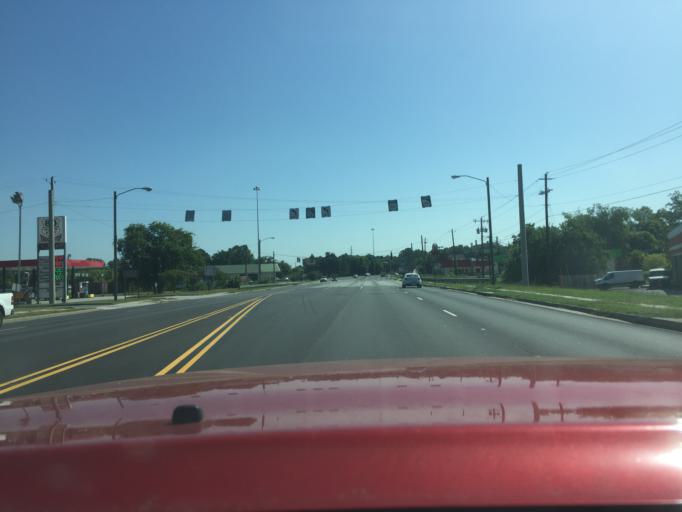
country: US
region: Georgia
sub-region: Chatham County
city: Garden City
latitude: 32.0958
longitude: -81.1445
